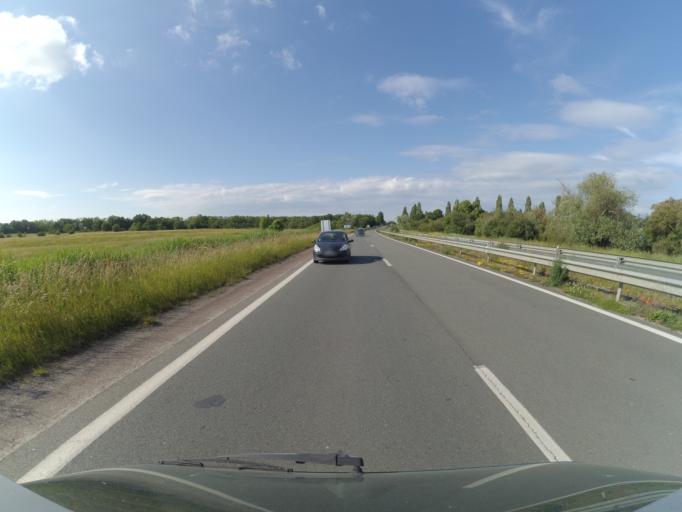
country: FR
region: Poitou-Charentes
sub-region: Departement de la Charente-Maritime
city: Saint-Agnant
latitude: 45.8697
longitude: -0.9694
